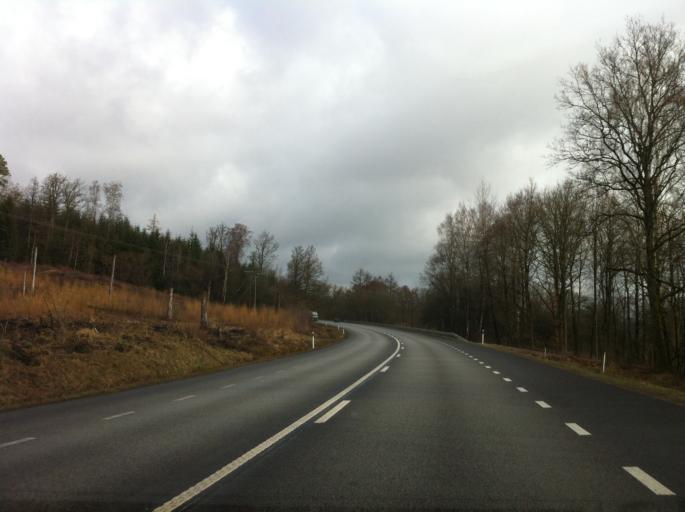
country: SE
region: Halland
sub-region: Halmstads Kommun
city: Aled
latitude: 56.7519
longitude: 12.9413
